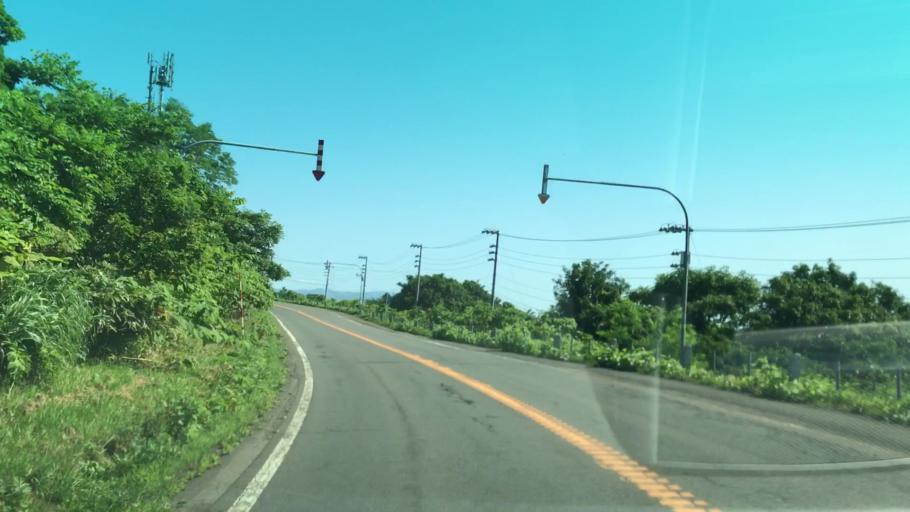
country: JP
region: Hokkaido
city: Iwanai
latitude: 43.1371
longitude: 140.4298
